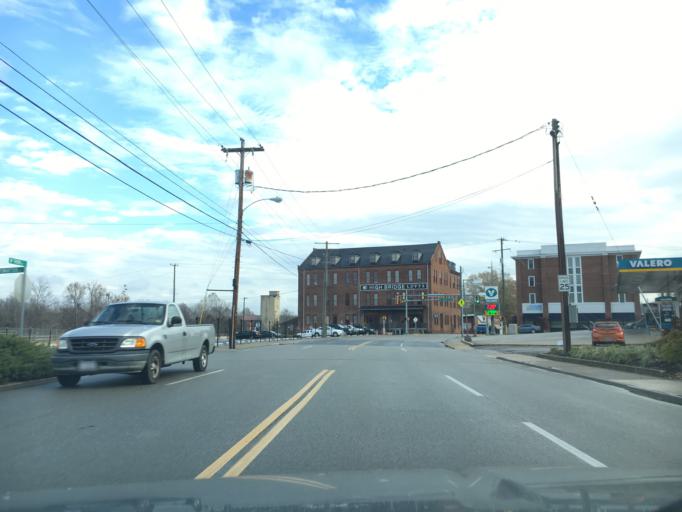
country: US
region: Virginia
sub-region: Prince Edward County
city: Farmville
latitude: 37.3042
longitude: -78.3967
